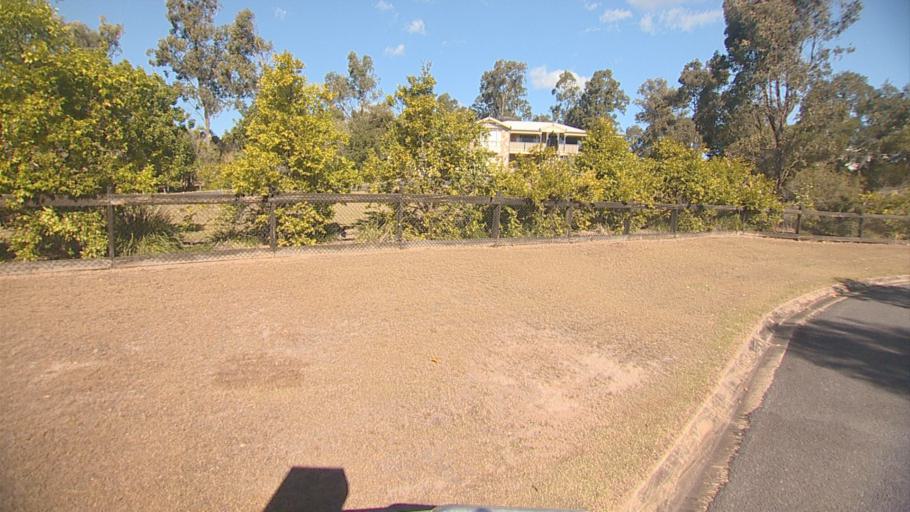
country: AU
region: Queensland
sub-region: Ipswich
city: Springfield Lakes
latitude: -27.7307
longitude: 152.9116
